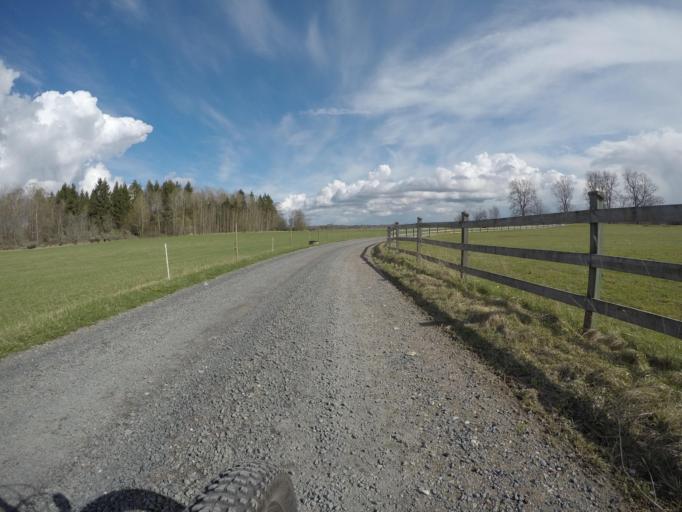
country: SE
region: Vaestmanland
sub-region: Kungsors Kommun
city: Kungsoer
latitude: 59.2833
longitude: 16.1524
